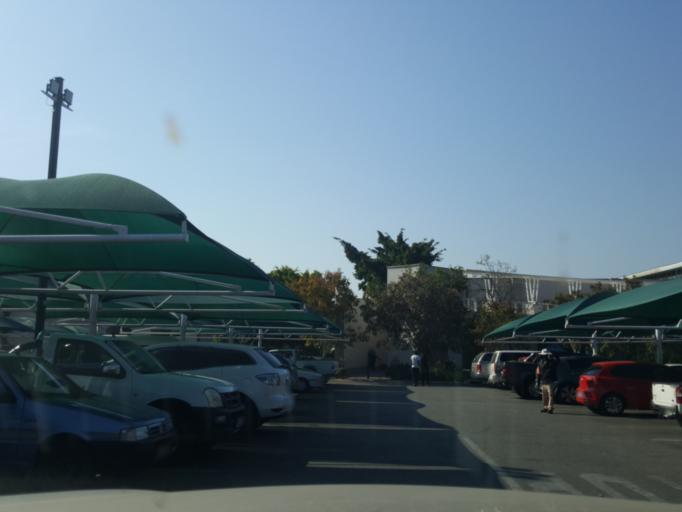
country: ZA
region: Mpumalanga
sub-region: Ehlanzeni District
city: Nelspruit
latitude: -25.4367
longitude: 30.9663
